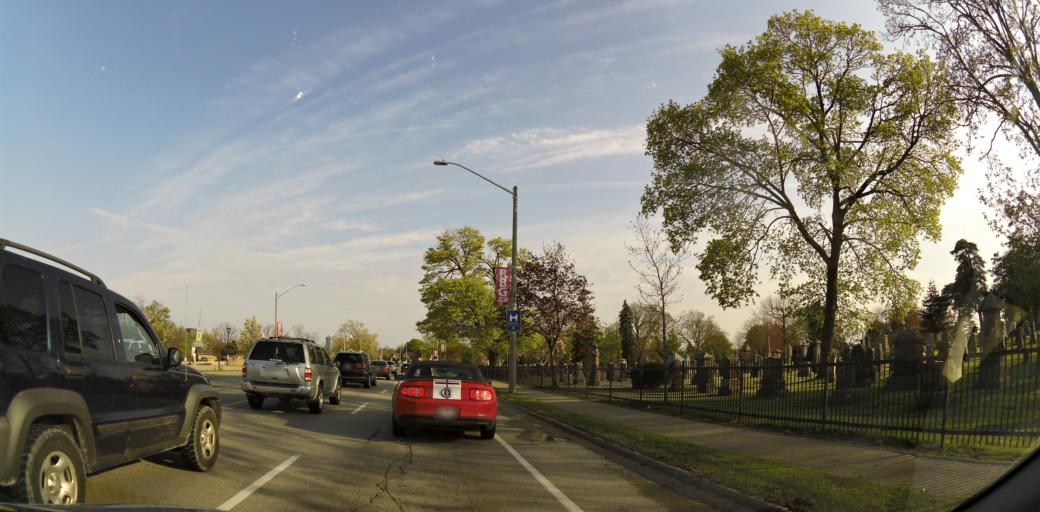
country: CA
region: Ontario
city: Hamilton
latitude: 43.2708
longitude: -79.8865
